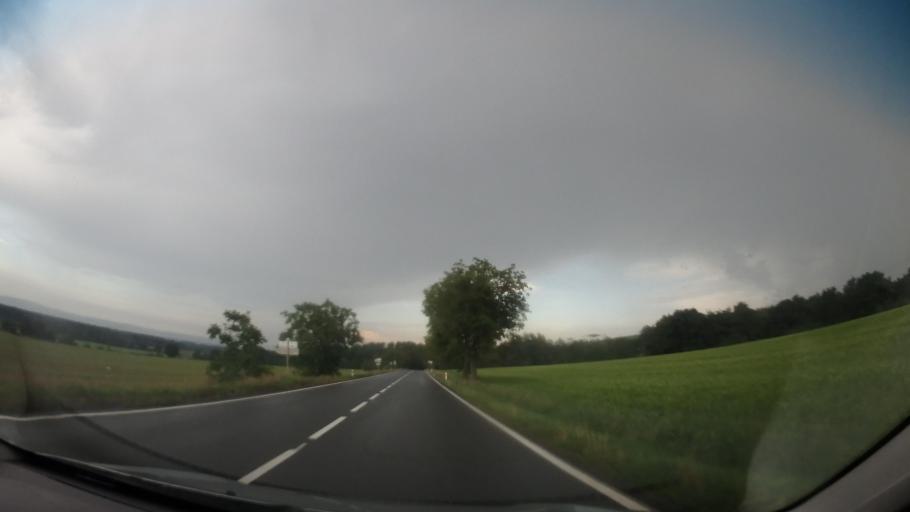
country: CZ
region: Olomoucky
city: Bila Lhota
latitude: 49.7012
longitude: 17.0101
